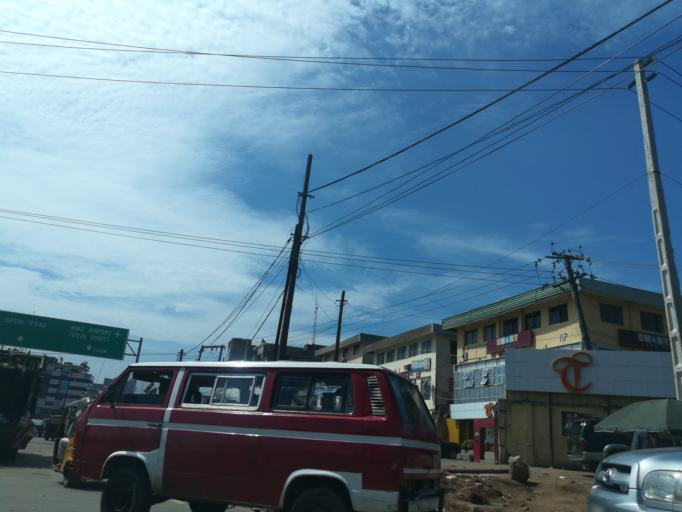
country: NG
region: Lagos
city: Ikeja
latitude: 6.6069
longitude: 3.3491
